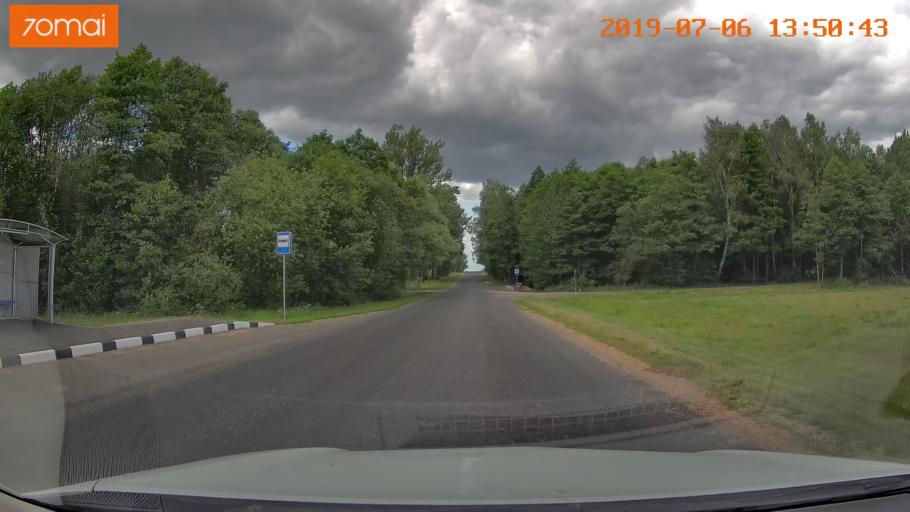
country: BY
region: Minsk
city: Ivyanyets
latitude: 53.7018
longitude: 26.8407
